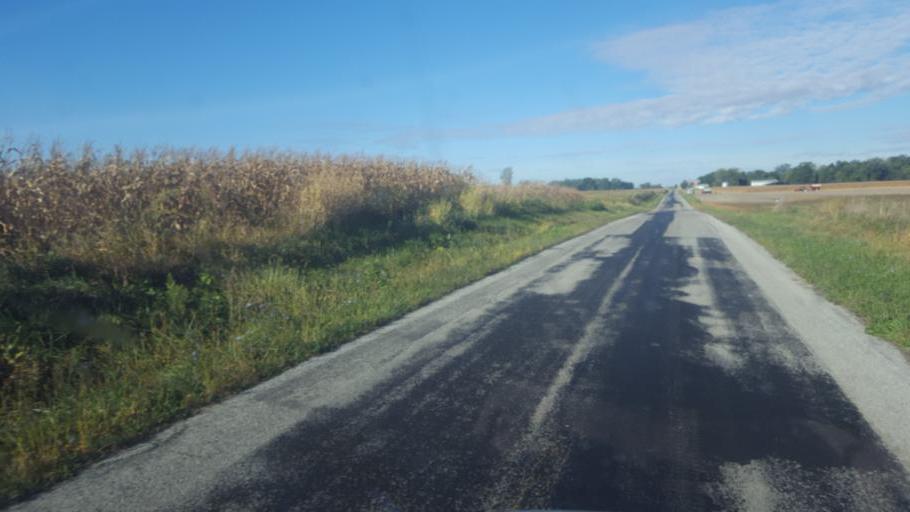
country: US
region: Ohio
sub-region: Crawford County
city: Bucyrus
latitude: 40.6888
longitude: -82.9636
